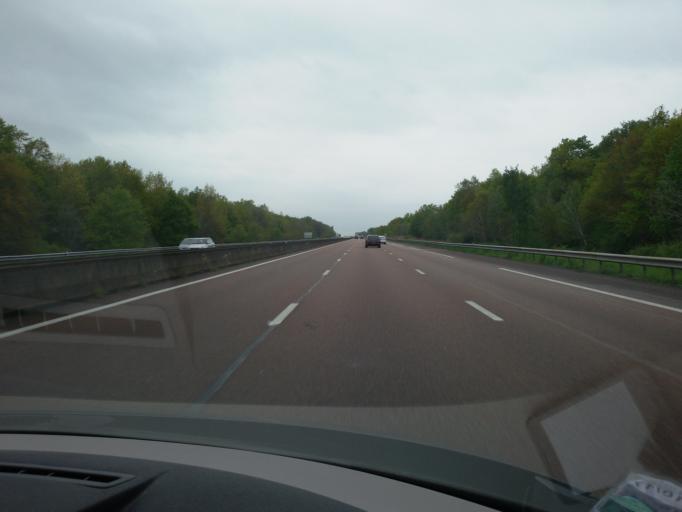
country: FR
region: Bourgogne
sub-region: Departement de Saone-et-Loire
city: Varennes-le-Grand
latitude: 46.7039
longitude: 4.8420
